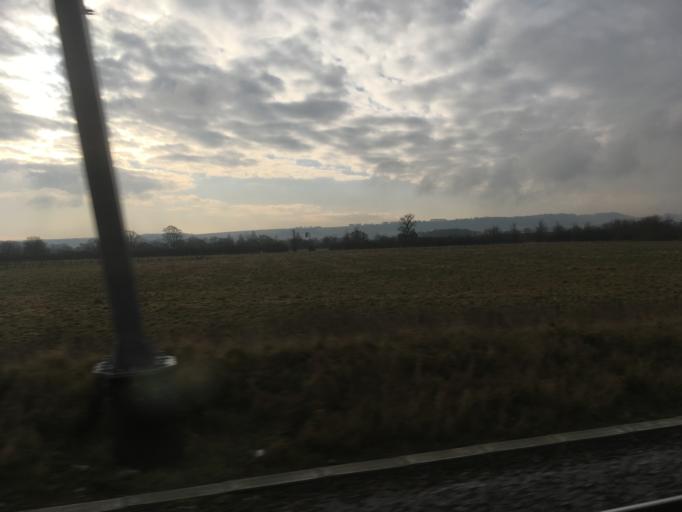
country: GB
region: England
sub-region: Wiltshire
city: Lydiard Tregoze
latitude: 51.5442
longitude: -1.8319
